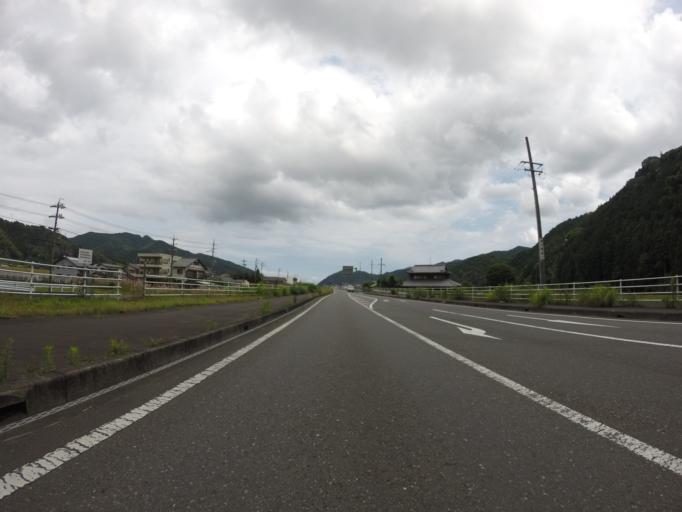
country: JP
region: Shizuoka
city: Shizuoka-shi
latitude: 34.9867
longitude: 138.2971
